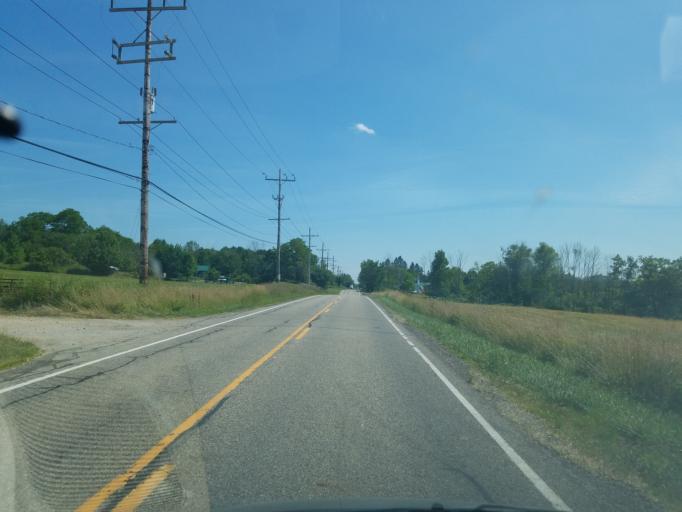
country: US
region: Ohio
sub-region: Geauga County
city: Burton
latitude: 41.5238
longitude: -81.1443
